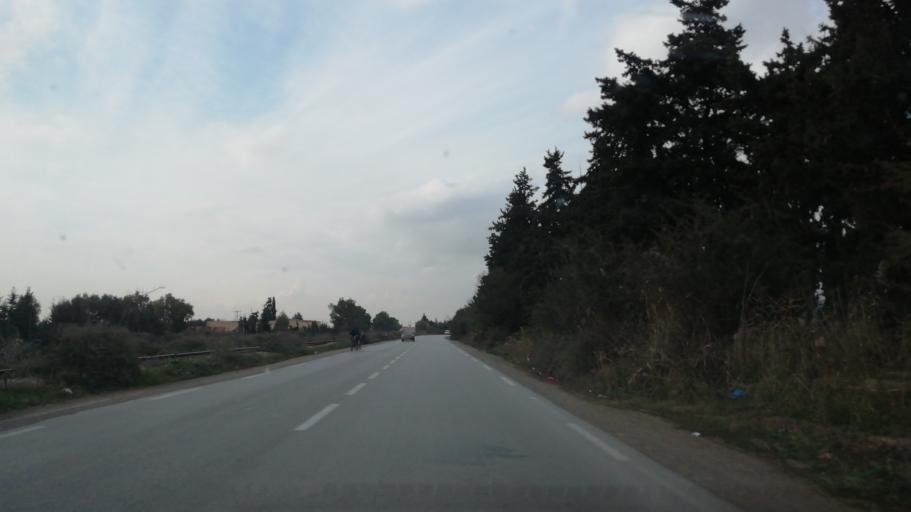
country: DZ
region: Mascara
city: Sig
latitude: 35.6652
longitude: 0.0022
